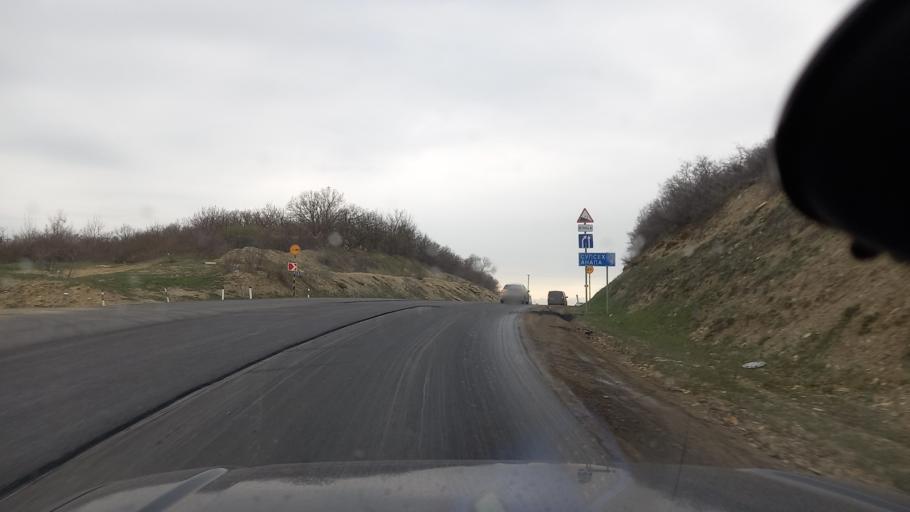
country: RU
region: Krasnodarskiy
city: Anapskaya
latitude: 44.8441
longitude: 37.3767
